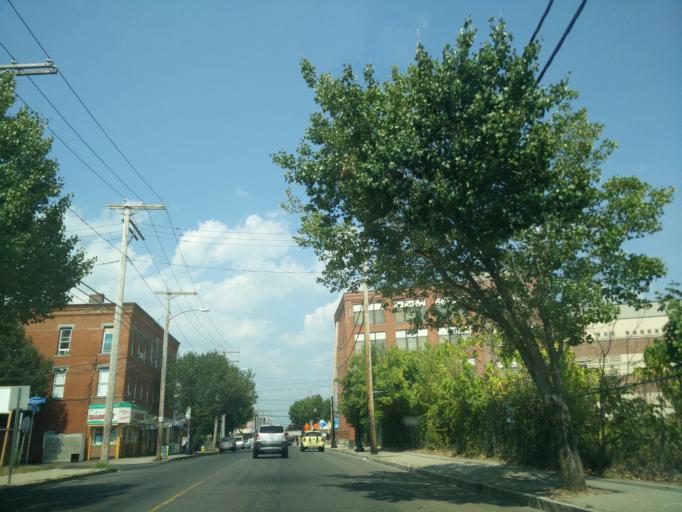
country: US
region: Connecticut
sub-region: Fairfield County
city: Bridgeport
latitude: 41.1841
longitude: -73.1809
